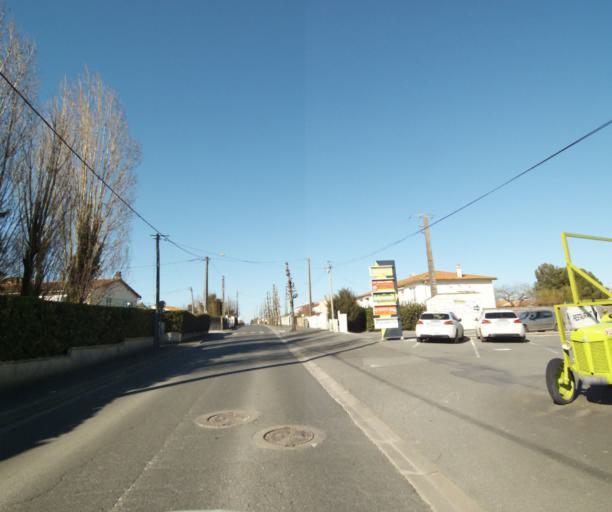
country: FR
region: Poitou-Charentes
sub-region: Departement des Deux-Sevres
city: Niort
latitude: 46.3524
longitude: -0.4790
